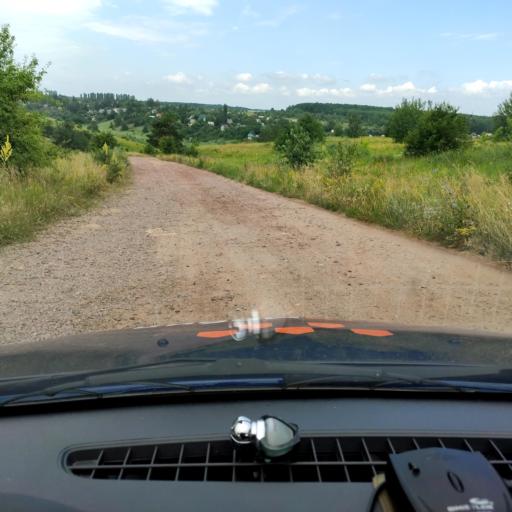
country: RU
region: Voronezj
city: Ramon'
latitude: 52.0734
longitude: 39.3230
